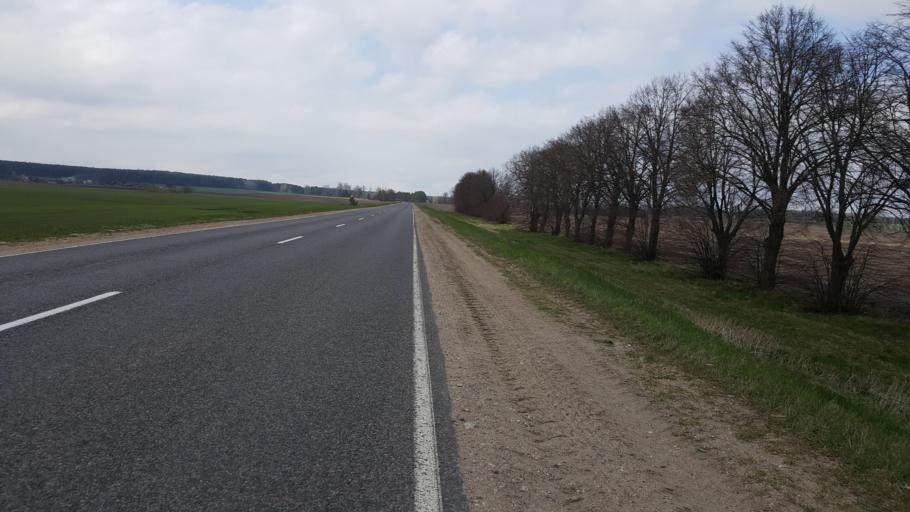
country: BY
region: Brest
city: Kamyanyets
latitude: 52.3633
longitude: 23.8897
